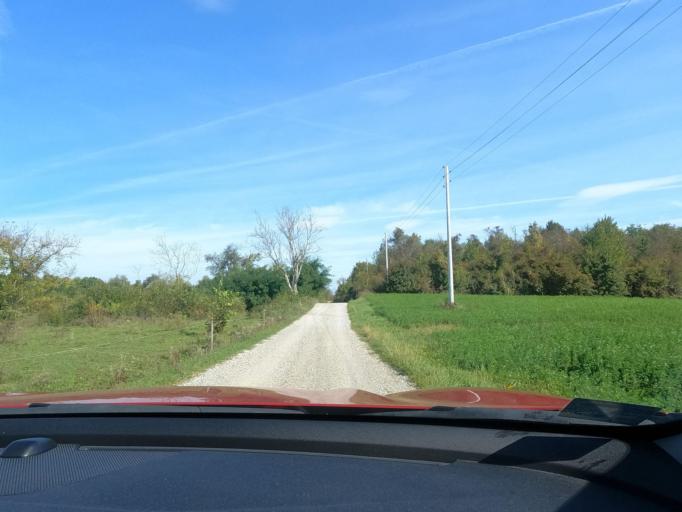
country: HR
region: Sisacko-Moslavacka
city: Glina
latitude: 45.3355
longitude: 16.2088
